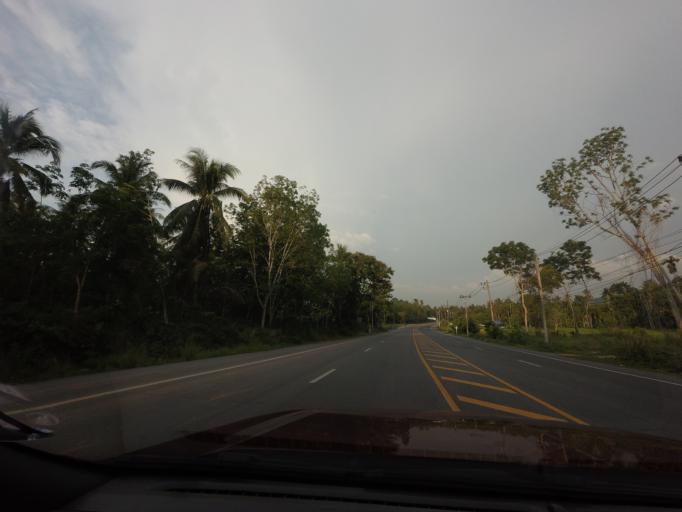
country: TH
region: Pattani
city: Khok Pho
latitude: 6.6774
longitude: 101.1221
